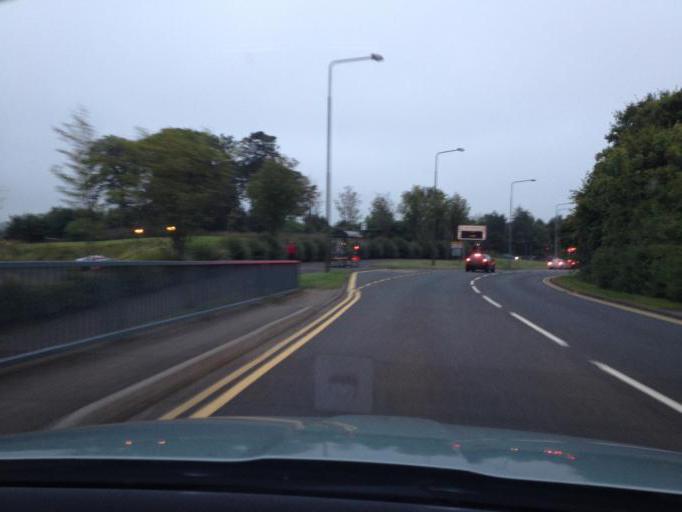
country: GB
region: Scotland
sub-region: West Lothian
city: Livingston
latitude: 55.8918
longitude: -3.5265
